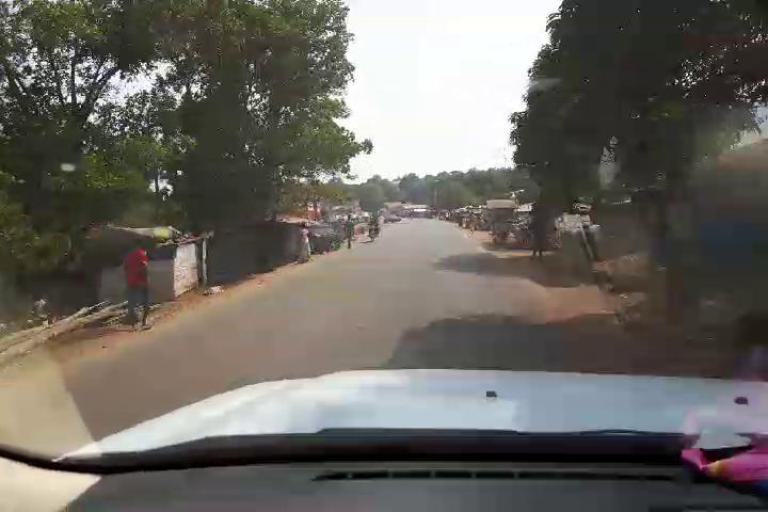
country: SL
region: Western Area
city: Waterloo
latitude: 8.2098
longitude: -13.1038
